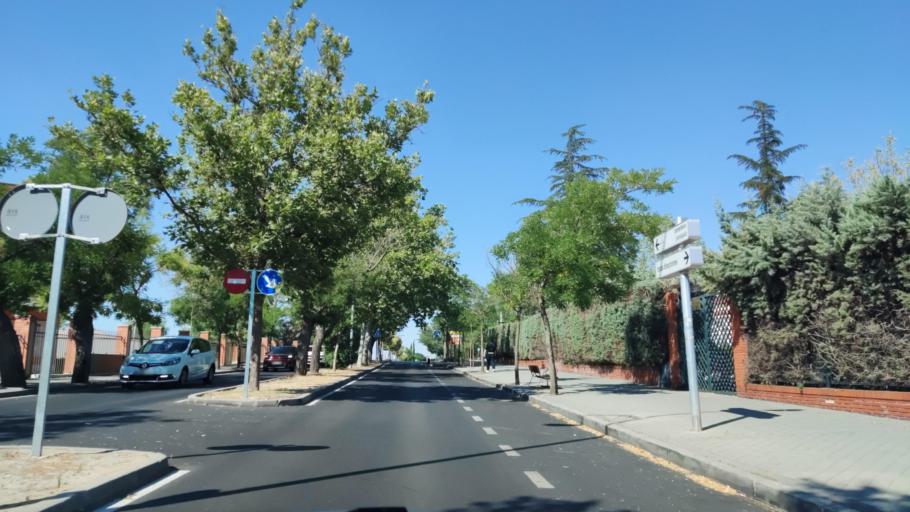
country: ES
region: Madrid
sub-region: Provincia de Madrid
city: Leganes
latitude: 40.3405
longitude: -3.7634
